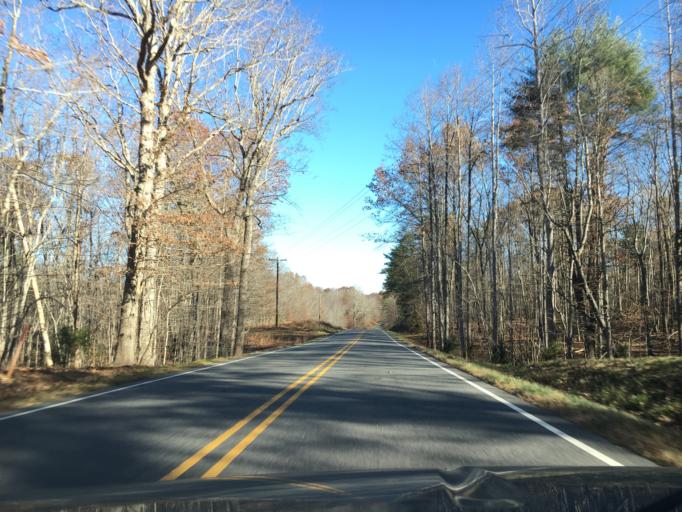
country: US
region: Virginia
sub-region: Buckingham County
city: Buckingham
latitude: 37.4715
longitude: -78.6600
